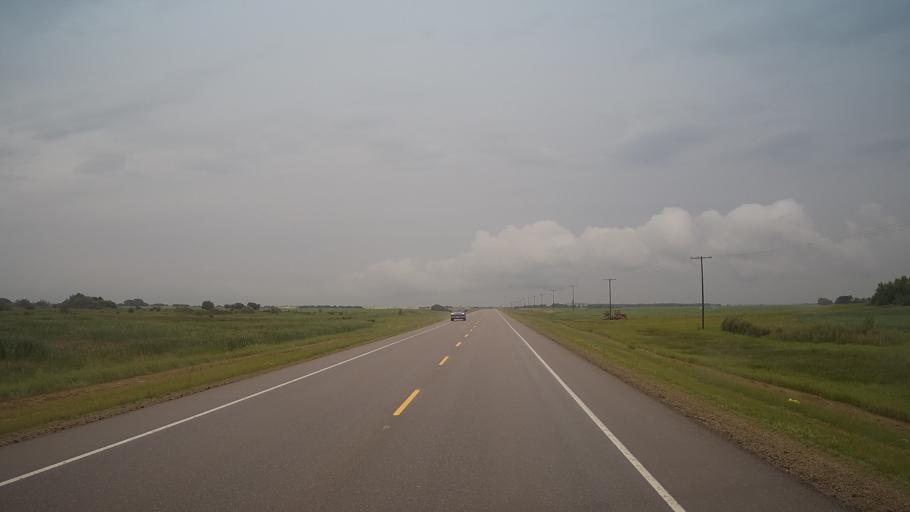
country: CA
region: Saskatchewan
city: Wilkie
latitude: 52.3197
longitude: -108.7015
